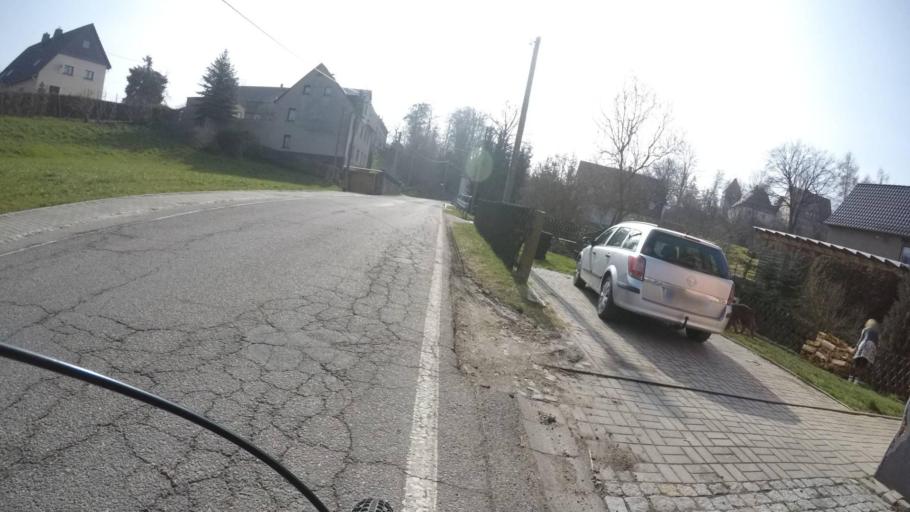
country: DE
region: Saxony
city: Niederfrohna
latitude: 50.8919
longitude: 12.6813
